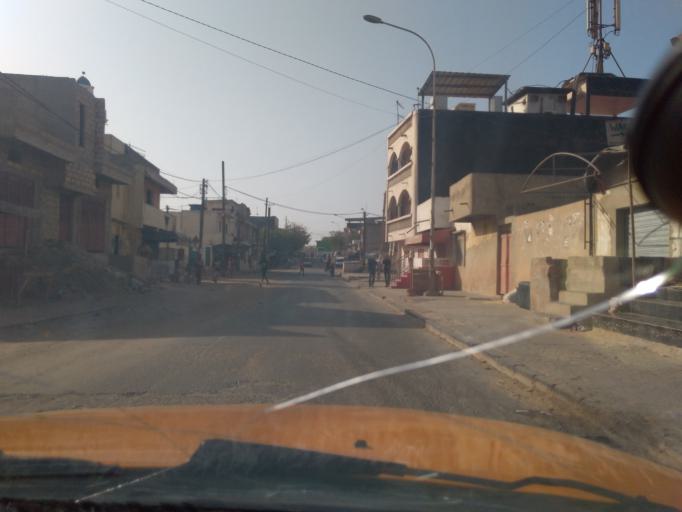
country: SN
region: Dakar
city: Grand Dakar
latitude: 14.7391
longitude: -17.4459
